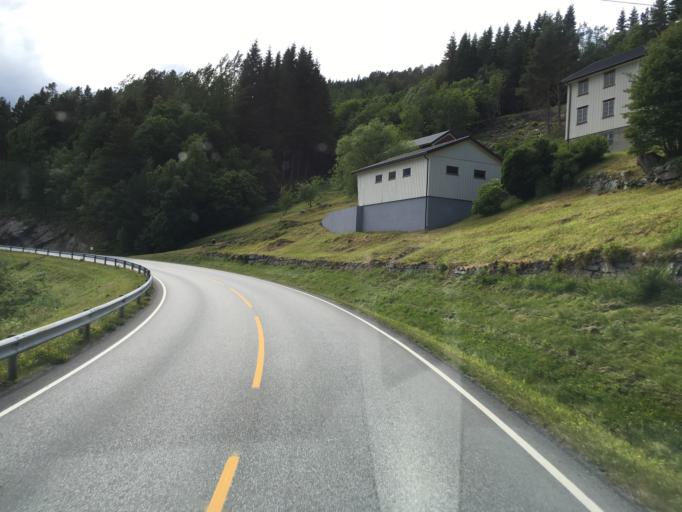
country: NO
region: More og Romsdal
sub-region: Tingvoll
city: Tingvoll
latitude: 62.9760
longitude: 8.0655
